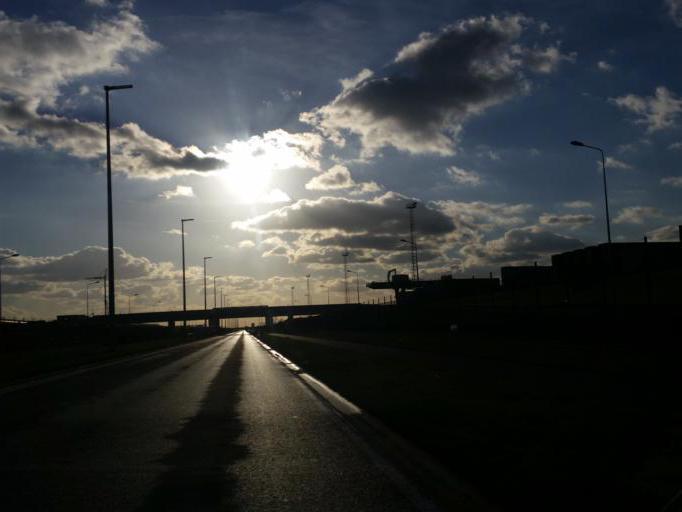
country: BE
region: Flanders
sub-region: Provincie Oost-Vlaanderen
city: Beveren
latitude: 51.2918
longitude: 4.2482
